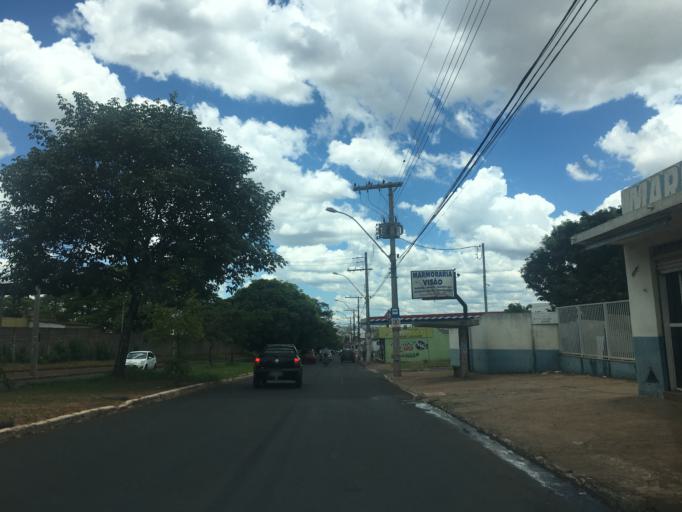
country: BR
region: Minas Gerais
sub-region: Uberlandia
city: Uberlandia
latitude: -18.9369
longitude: -48.3058
